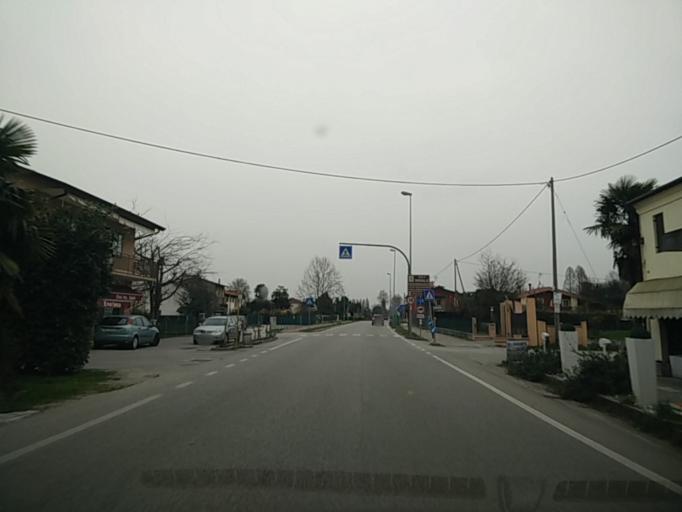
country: IT
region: Veneto
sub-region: Provincia di Padova
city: Massanzago-Ca' Baglioni-San Dono
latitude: 45.5542
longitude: 12.0332
